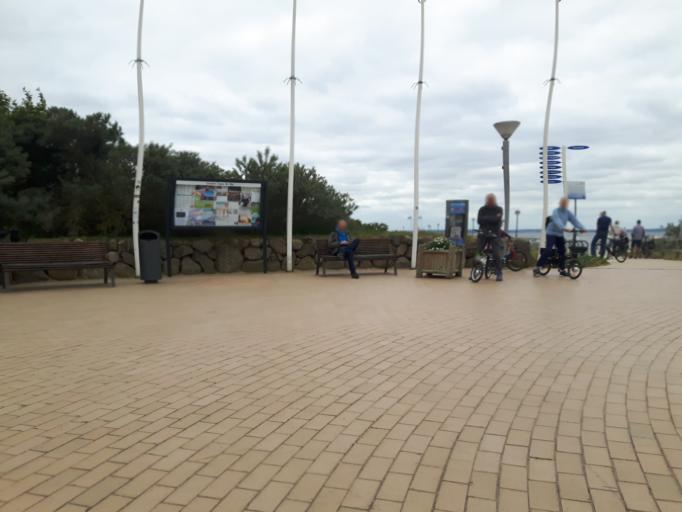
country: DE
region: Schleswig-Holstein
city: Neustadt in Holstein
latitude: 54.0890
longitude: 10.8583
